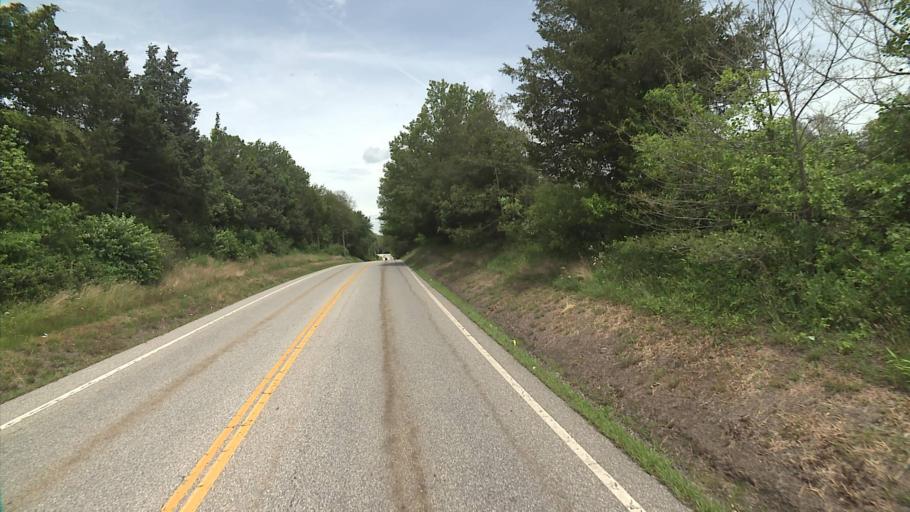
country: US
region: Connecticut
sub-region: New London County
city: Preston City
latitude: 41.5630
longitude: -71.9695
